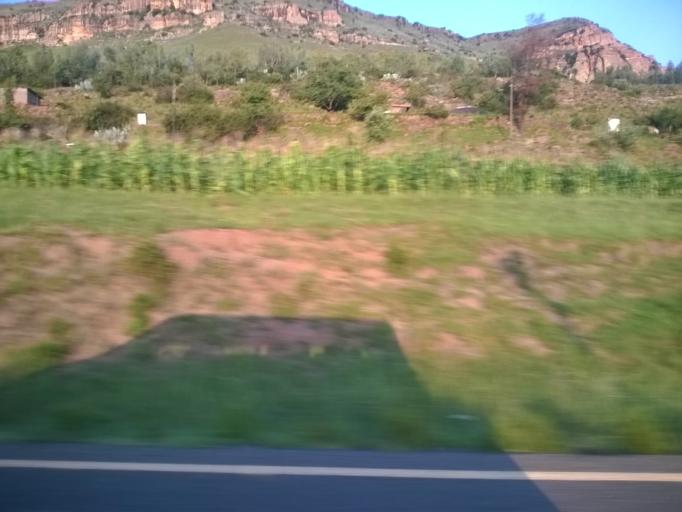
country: LS
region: Leribe
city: Leribe
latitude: -28.9657
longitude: 28.1729
